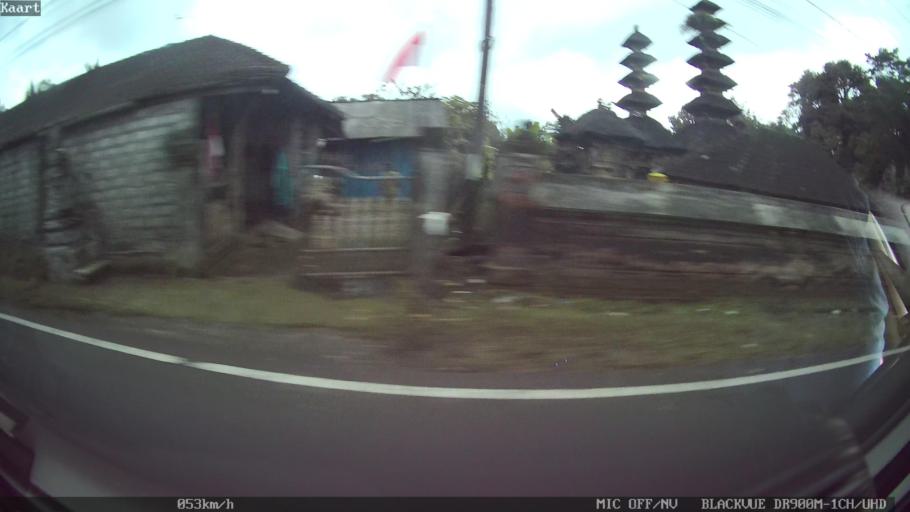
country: ID
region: Bali
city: Empalan
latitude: -8.3934
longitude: 115.1516
